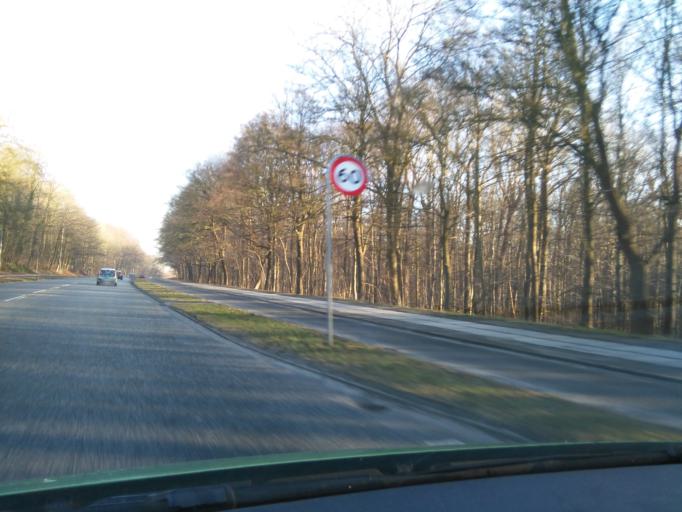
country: DK
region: Central Jutland
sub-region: Arhus Kommune
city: Arhus
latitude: 56.1210
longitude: 10.2072
